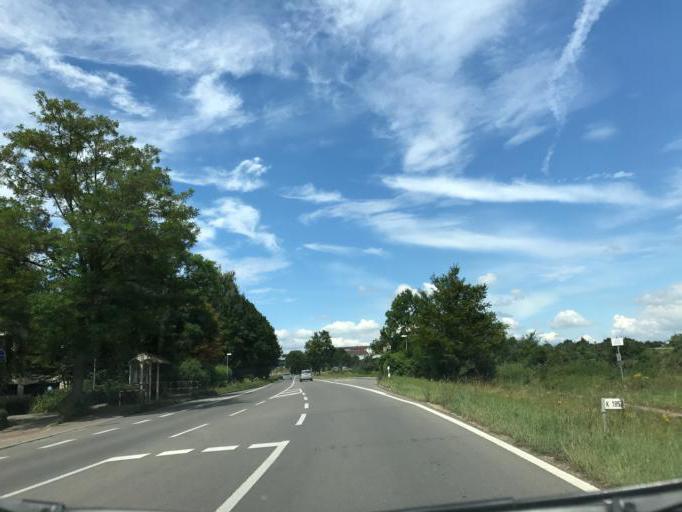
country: DE
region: Baden-Wuerttemberg
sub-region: Regierungsbezirk Stuttgart
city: Weinstadt-Endersbach
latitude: 48.8038
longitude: 9.3328
